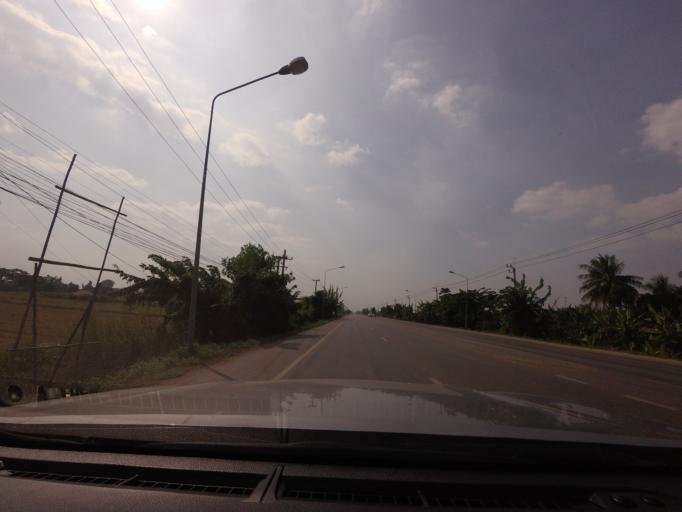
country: TH
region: Phitsanulok
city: Bang Rakam
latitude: 16.7724
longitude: 100.1681
